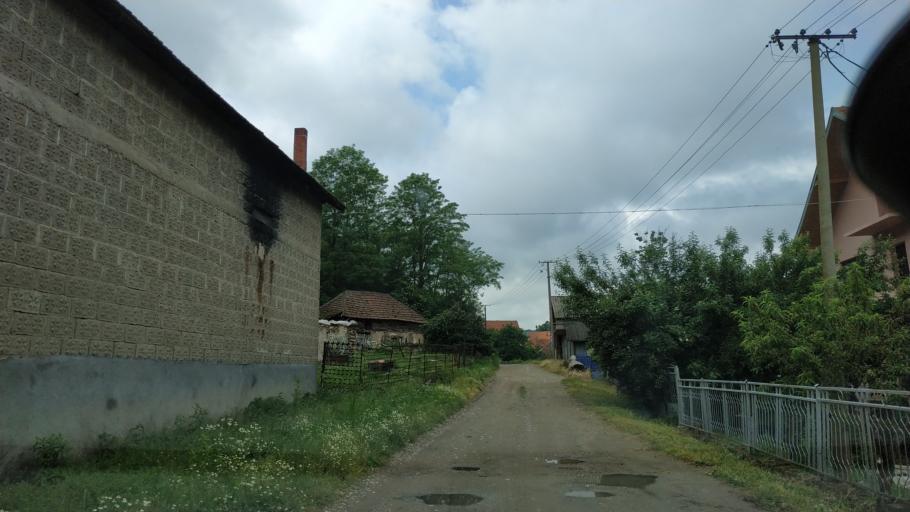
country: RS
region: Central Serbia
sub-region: Nisavski Okrug
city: Aleksinac
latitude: 43.4305
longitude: 21.6551
